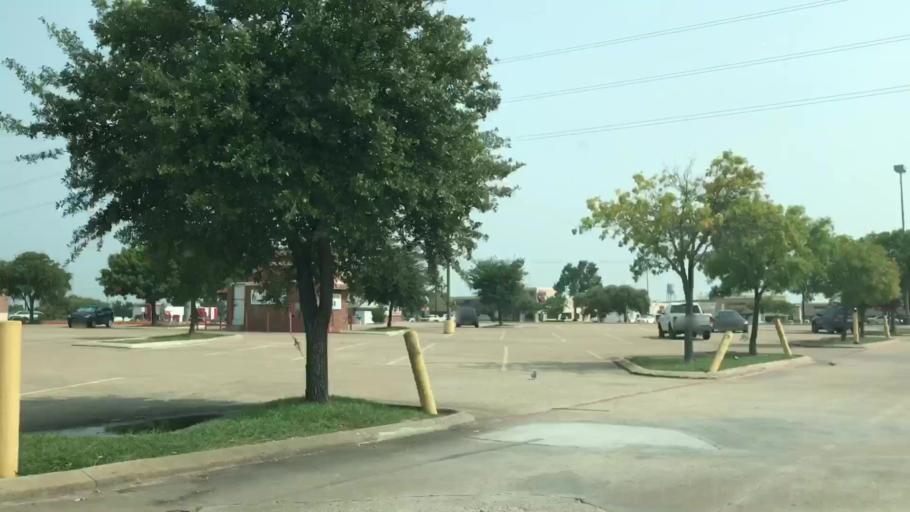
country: US
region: Texas
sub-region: Dallas County
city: Rowlett
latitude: 32.9086
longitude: -96.5680
